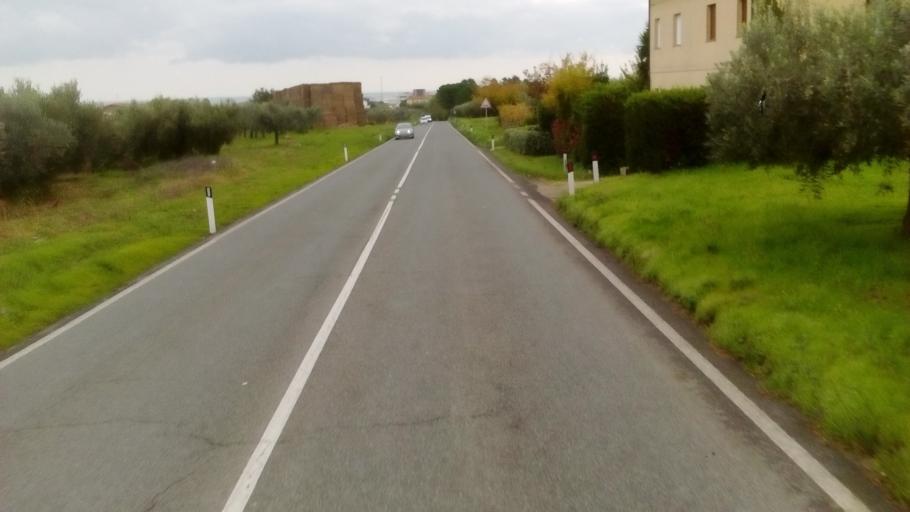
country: IT
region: Abruzzo
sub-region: Provincia di Chieti
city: Vasto
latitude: 42.1649
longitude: 14.6719
